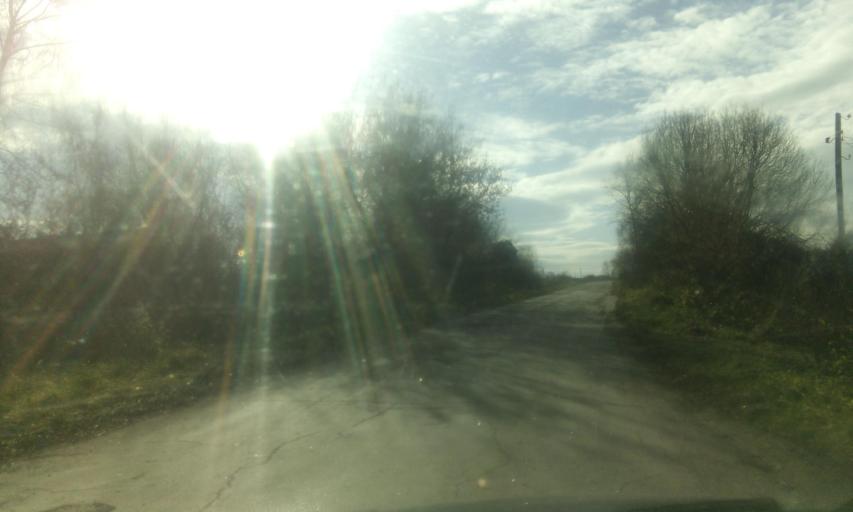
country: RU
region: Tula
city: Dubovka
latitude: 53.9446
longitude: 38.0369
